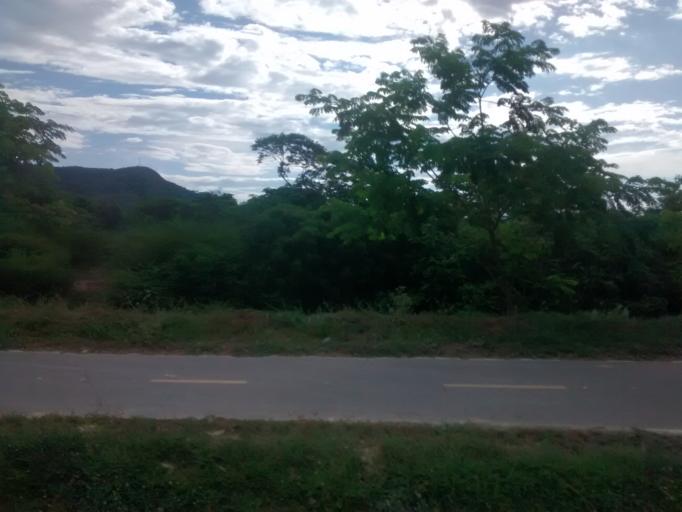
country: CO
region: Cundinamarca
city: Ricaurte
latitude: 4.2567
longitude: -74.7463
